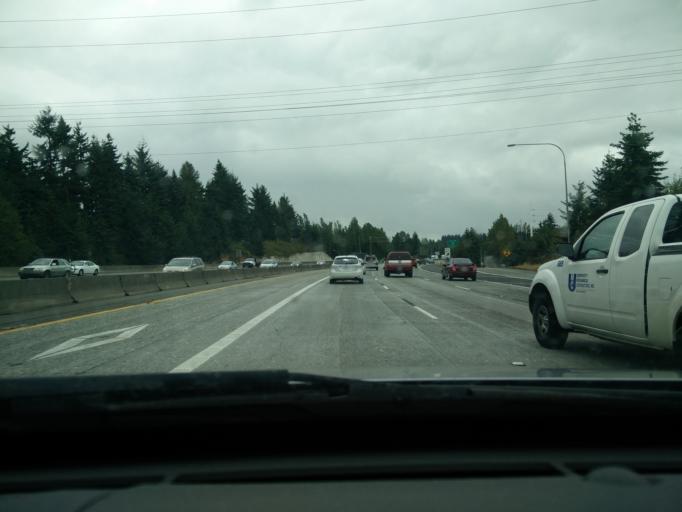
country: US
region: Washington
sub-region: King County
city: Shoreline
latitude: 47.7493
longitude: -122.3293
